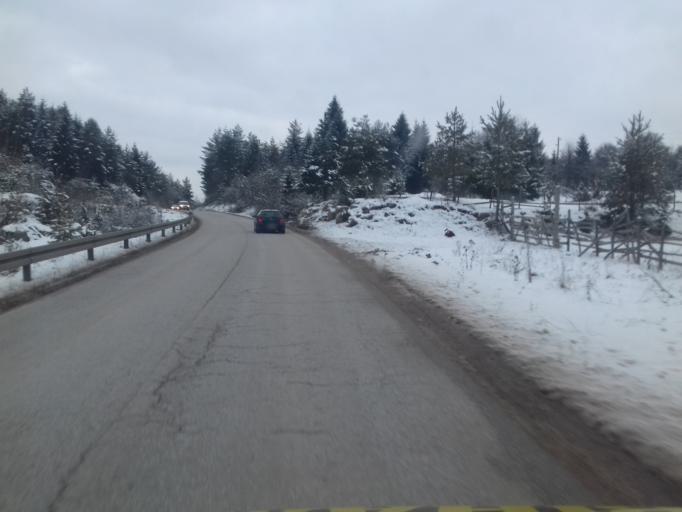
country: BA
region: Republika Srpska
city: Pale
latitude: 43.8732
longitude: 18.5710
